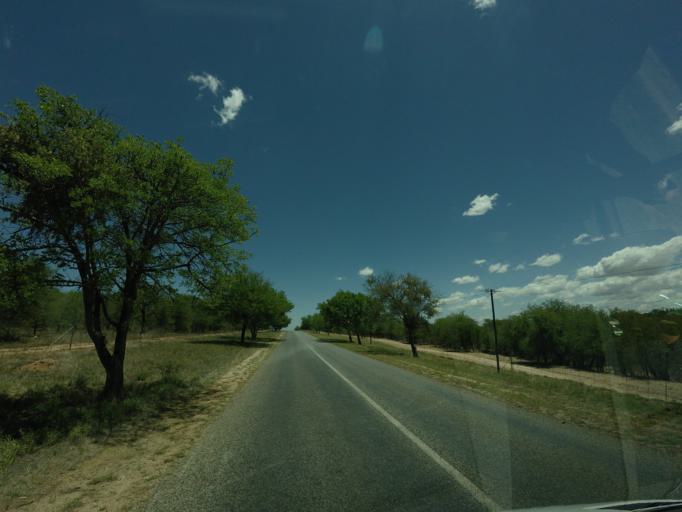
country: ZA
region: Limpopo
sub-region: Mopani District Municipality
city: Hoedspruit
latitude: -24.3751
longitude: 30.7331
